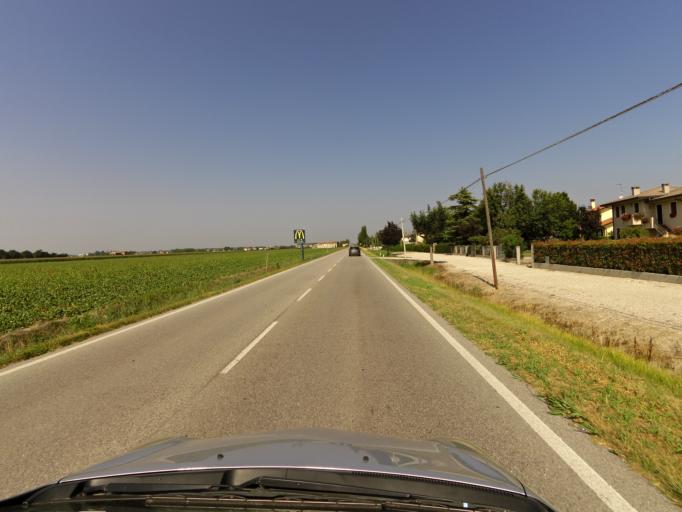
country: IT
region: Veneto
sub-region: Provincia di Venezia
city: Passarella
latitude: 45.6377
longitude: 12.6292
